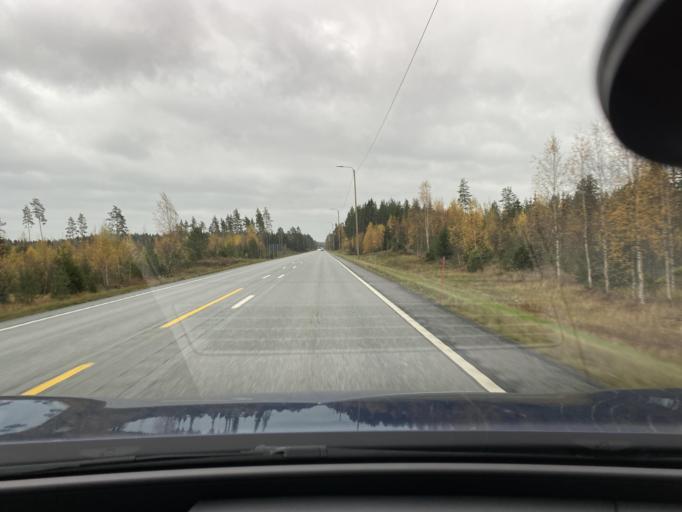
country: FI
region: Varsinais-Suomi
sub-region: Vakka-Suomi
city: Laitila
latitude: 60.9558
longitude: 21.5964
